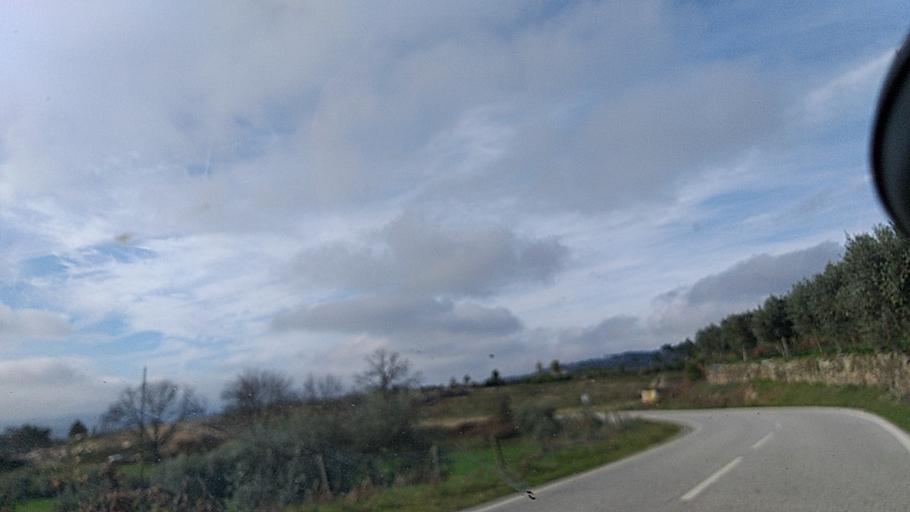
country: PT
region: Guarda
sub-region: Aguiar da Beira
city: Aguiar da Beira
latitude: 40.7465
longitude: -7.5546
